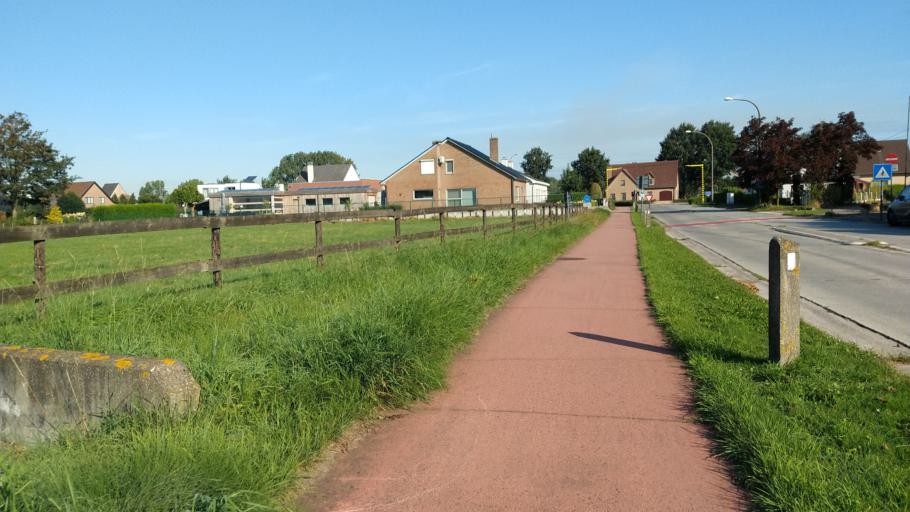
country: BE
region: Flanders
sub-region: Provincie Oost-Vlaanderen
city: Lochristi
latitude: 51.1204
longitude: 3.8298
